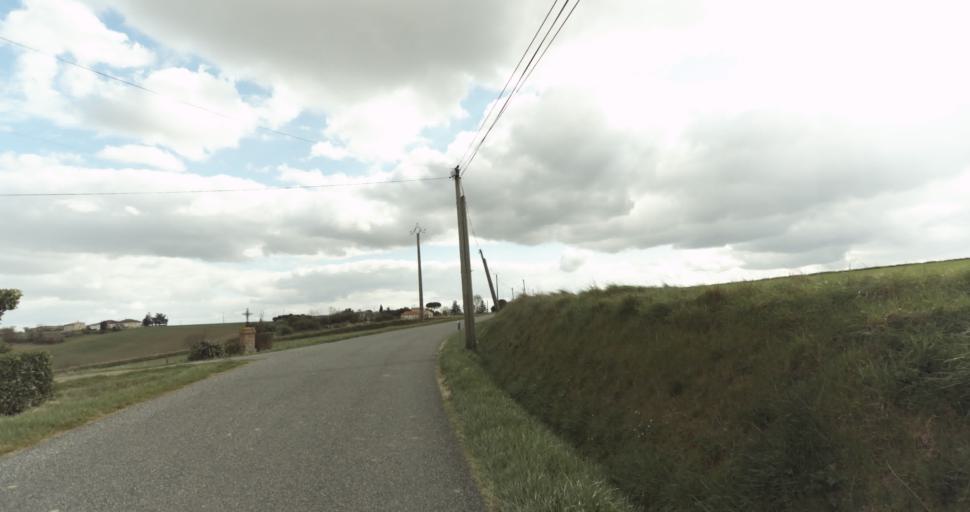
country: FR
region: Midi-Pyrenees
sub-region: Departement de la Haute-Garonne
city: Auterive
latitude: 43.3692
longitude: 1.4848
